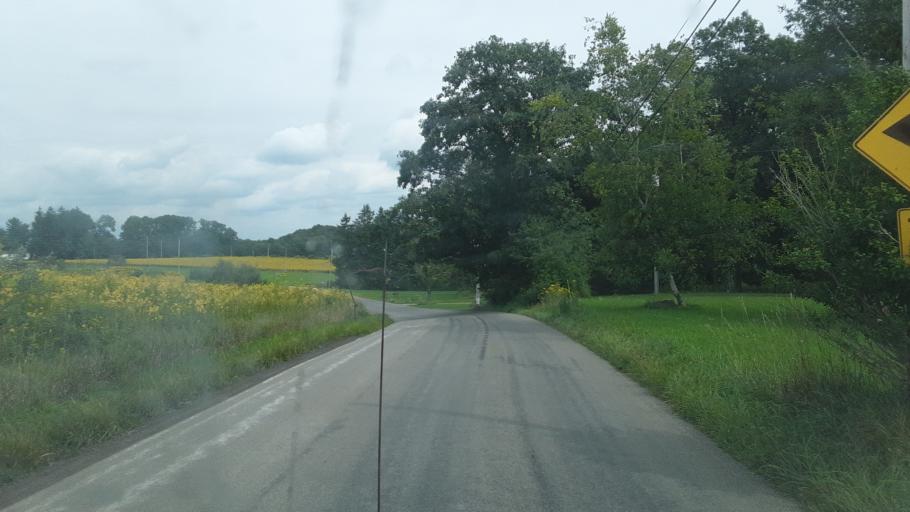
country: US
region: Pennsylvania
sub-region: Jefferson County
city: Punxsutawney
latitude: 40.9623
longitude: -79.1004
